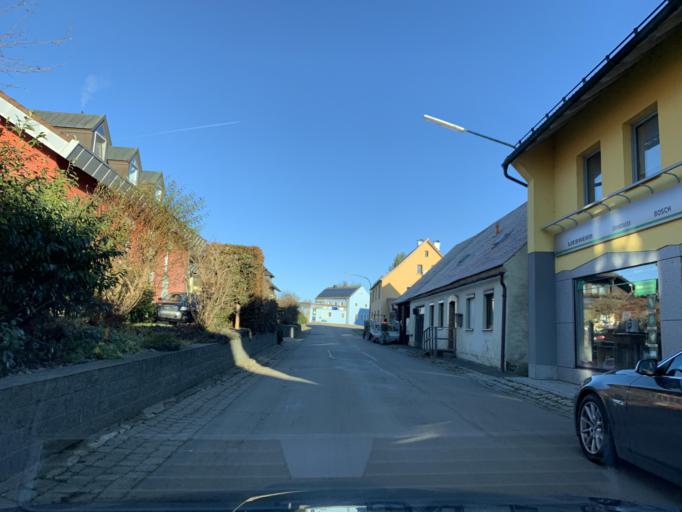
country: DE
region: Bavaria
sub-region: Upper Palatinate
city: Winklarn
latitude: 49.4290
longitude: 12.4814
